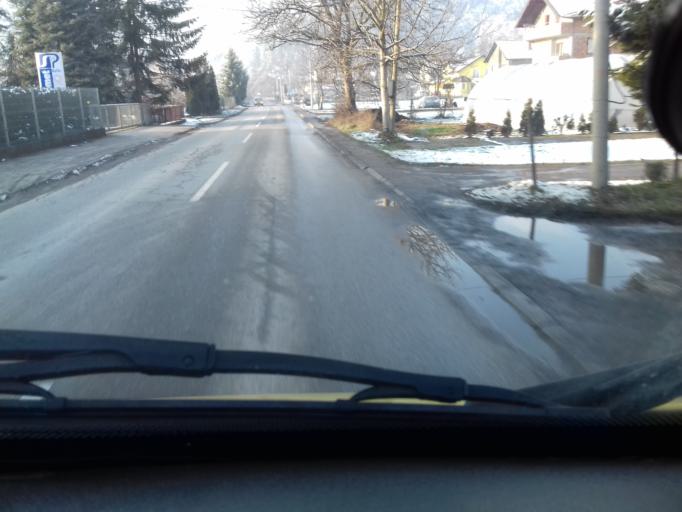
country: BA
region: Federation of Bosnia and Herzegovina
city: Mahala
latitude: 43.9962
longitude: 18.2189
